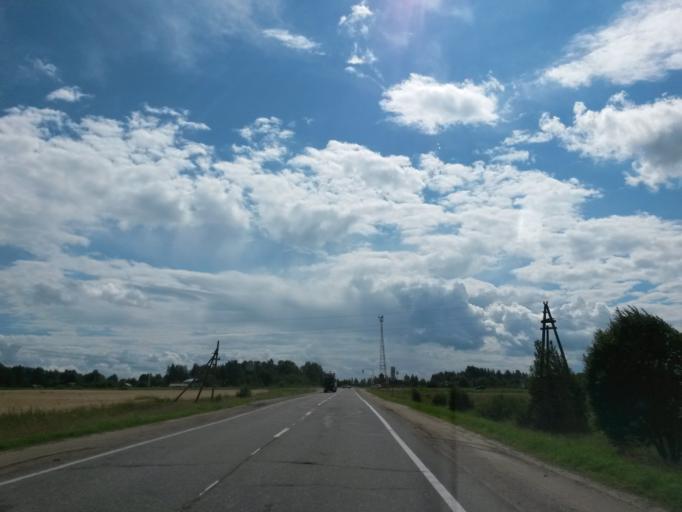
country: RU
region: Jaroslavl
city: Gavrilov-Yam
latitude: 57.3120
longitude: 39.9355
